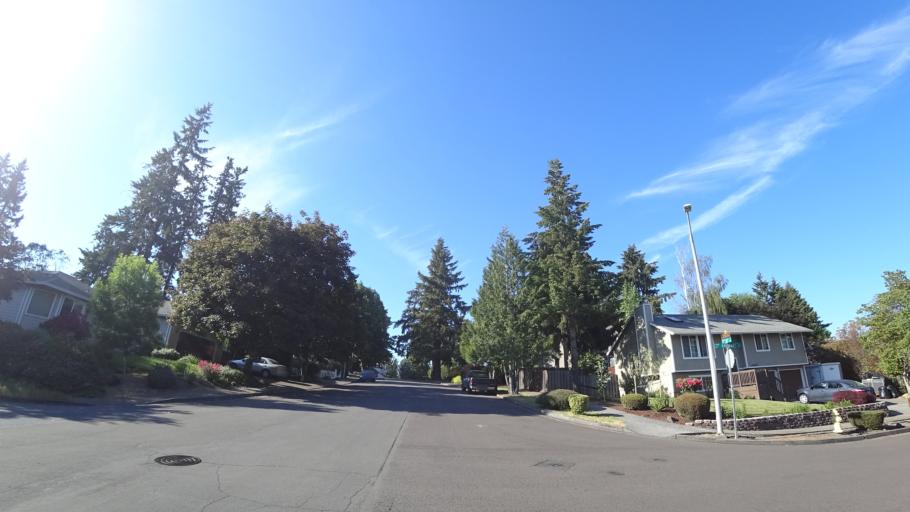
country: US
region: Oregon
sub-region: Washington County
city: Beaverton
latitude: 45.4627
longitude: -122.8119
